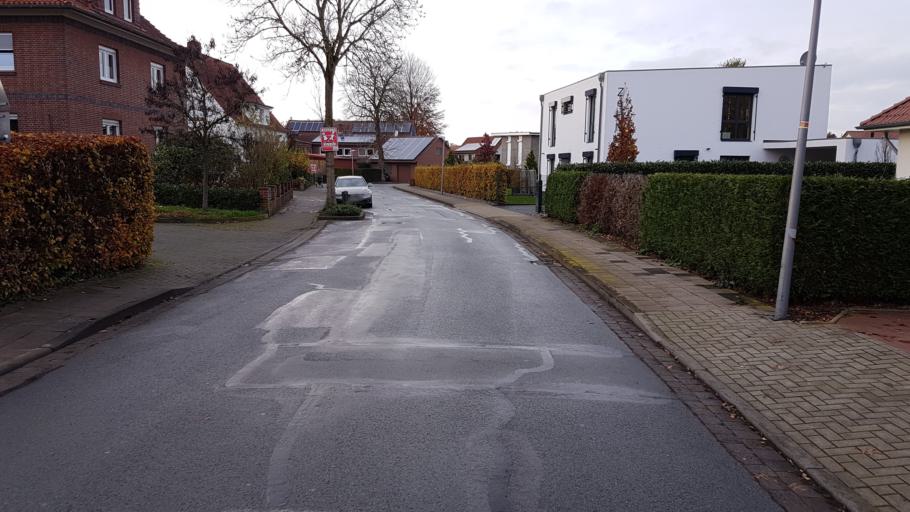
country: DE
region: North Rhine-Westphalia
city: Rahden
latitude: 52.4347
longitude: 8.6154
